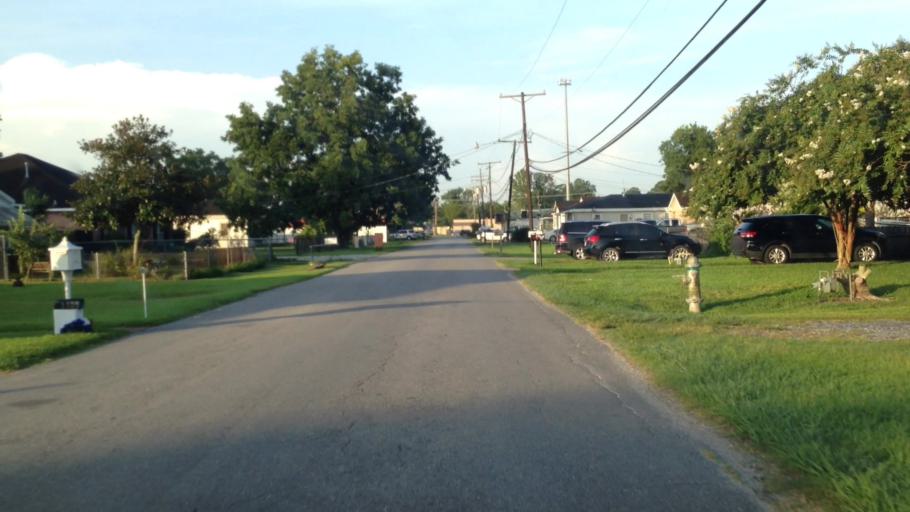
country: US
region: Louisiana
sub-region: Jefferson Parish
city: Bridge City
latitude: 29.9317
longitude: -90.1593
